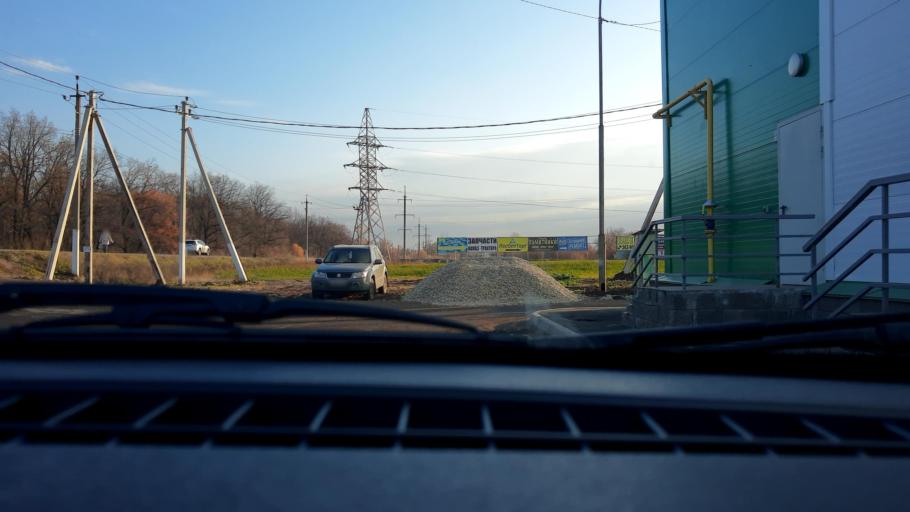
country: RU
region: Bashkortostan
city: Mikhaylovka
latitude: 54.8021
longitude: 55.8611
